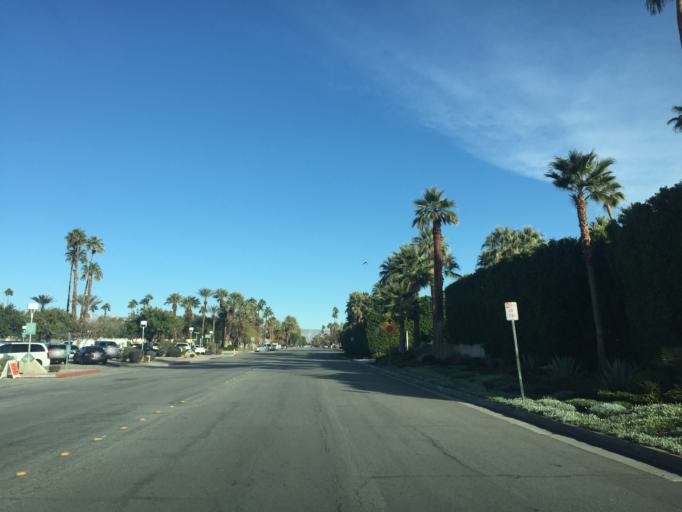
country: US
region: California
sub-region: Riverside County
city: Palm Springs
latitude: 33.8389
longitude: -116.5413
